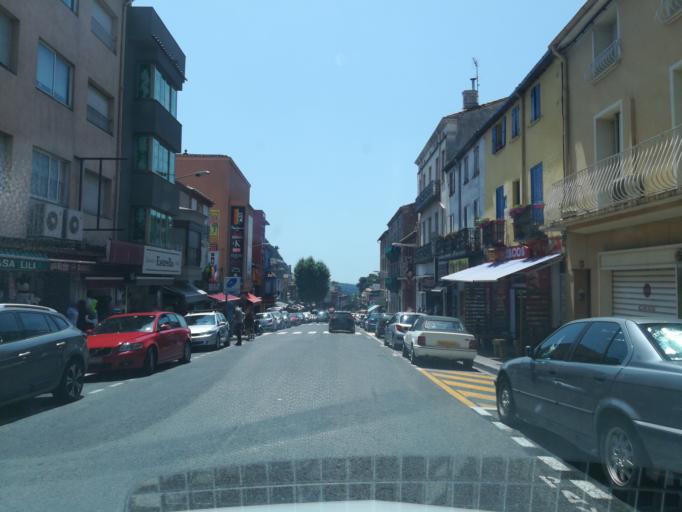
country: ES
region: Catalonia
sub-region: Provincia de Girona
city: la Jonquera
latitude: 42.4629
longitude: 2.8635
